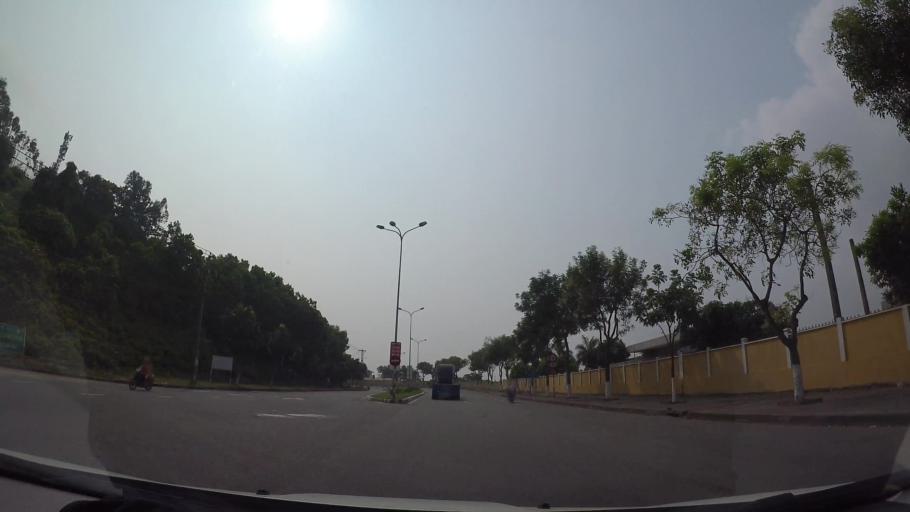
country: VN
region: Da Nang
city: Da Nang
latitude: 16.1186
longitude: 108.2245
